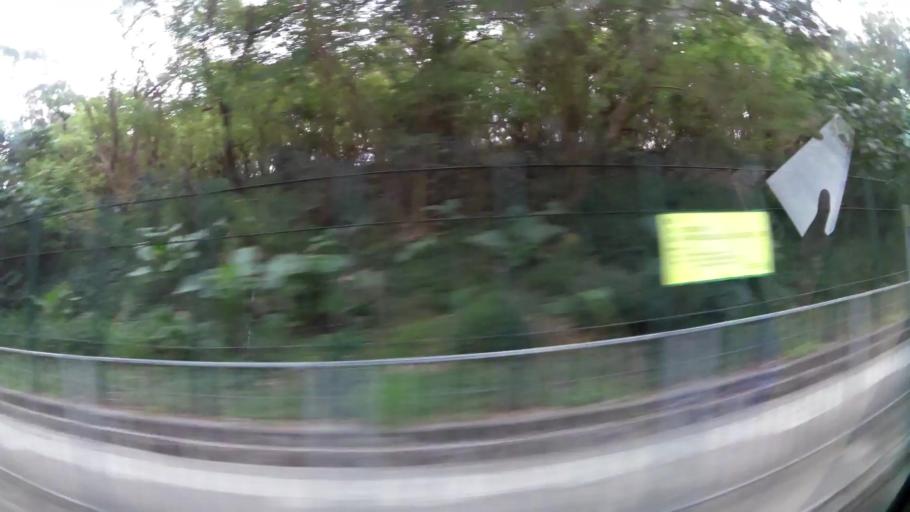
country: HK
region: Tsuen Wan
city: Tsuen Wan
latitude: 22.3568
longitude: 114.1185
